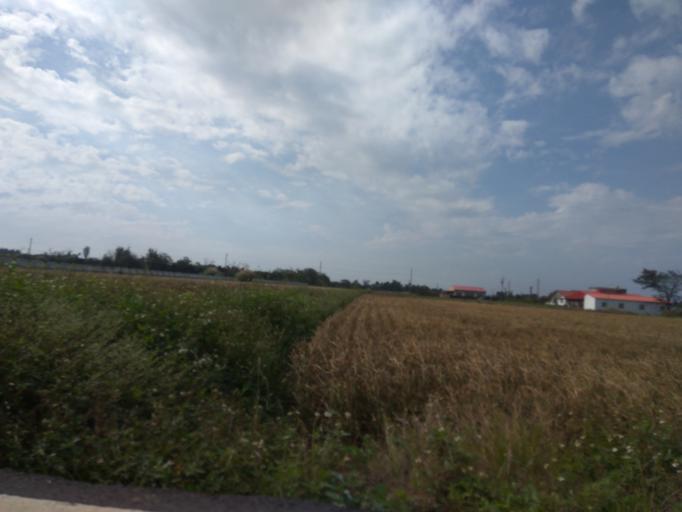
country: TW
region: Taiwan
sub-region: Hsinchu
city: Zhubei
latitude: 24.9548
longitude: 121.0082
